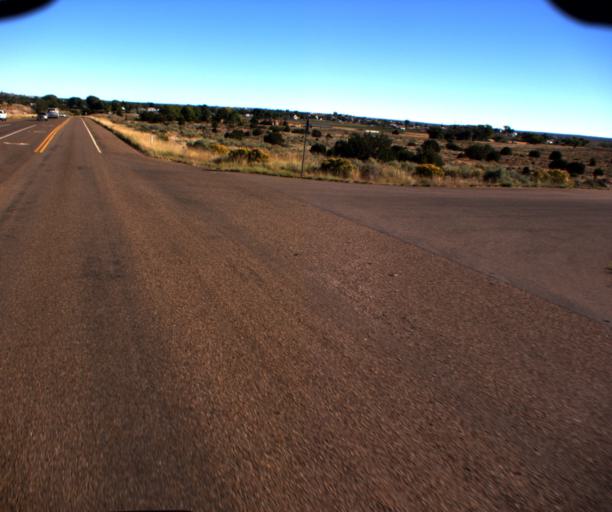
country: US
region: Arizona
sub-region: Navajo County
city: Taylor
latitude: 34.4478
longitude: -110.0935
